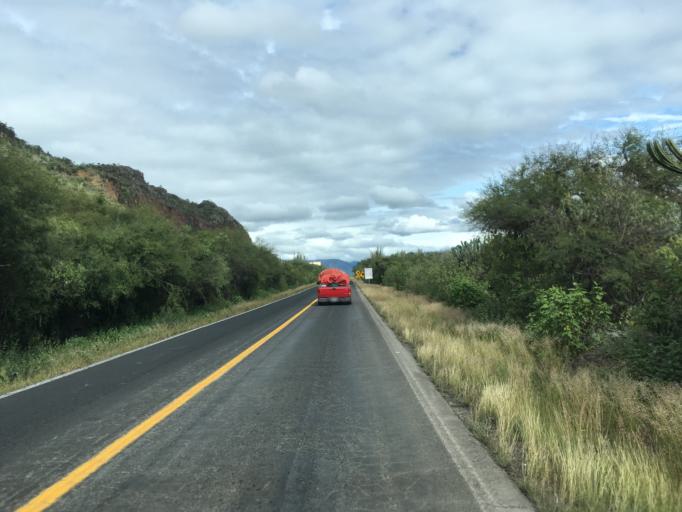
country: MX
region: Hidalgo
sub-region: San Agustin Metzquititlan
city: Mezquititlan
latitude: 20.4277
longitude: -98.6864
